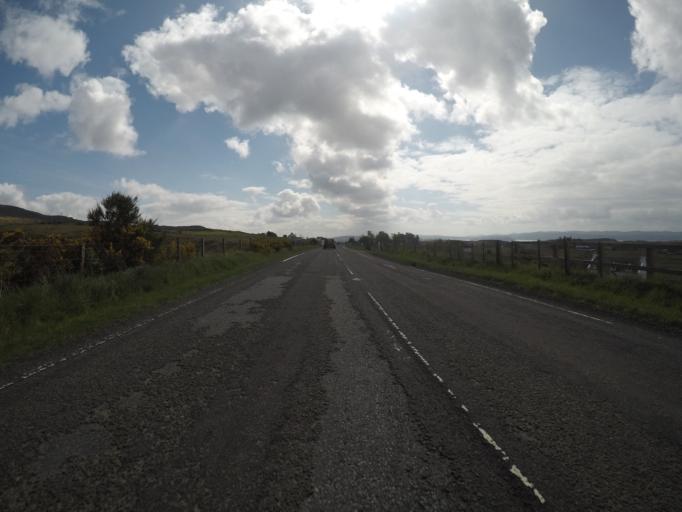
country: GB
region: Scotland
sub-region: Highland
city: Portree
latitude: 57.5682
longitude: -6.3645
